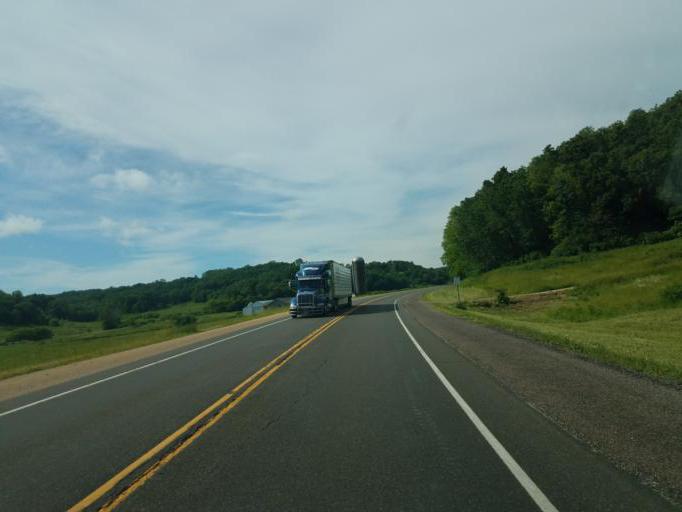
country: US
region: Wisconsin
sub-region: Monroe County
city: Tomah
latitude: 43.8768
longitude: -90.4806
